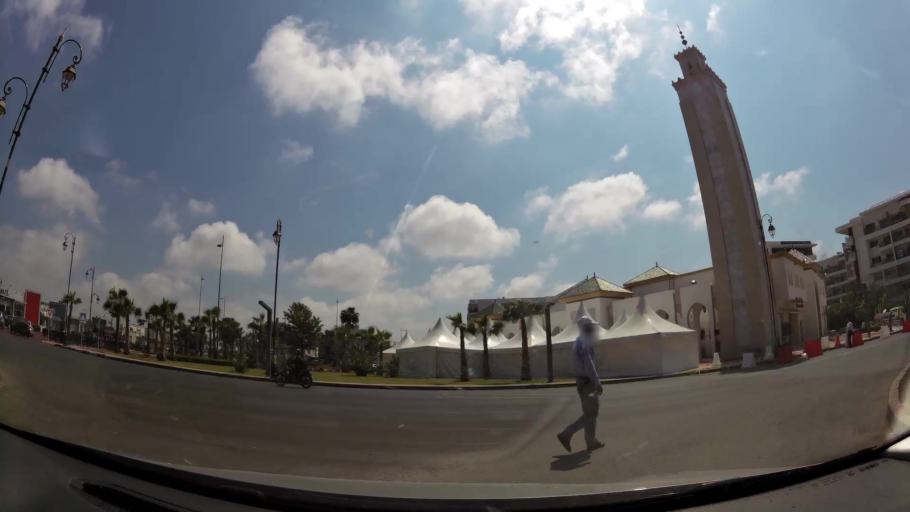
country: MA
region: Rabat-Sale-Zemmour-Zaer
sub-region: Skhirate-Temara
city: Temara
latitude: 33.9543
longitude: -6.8810
